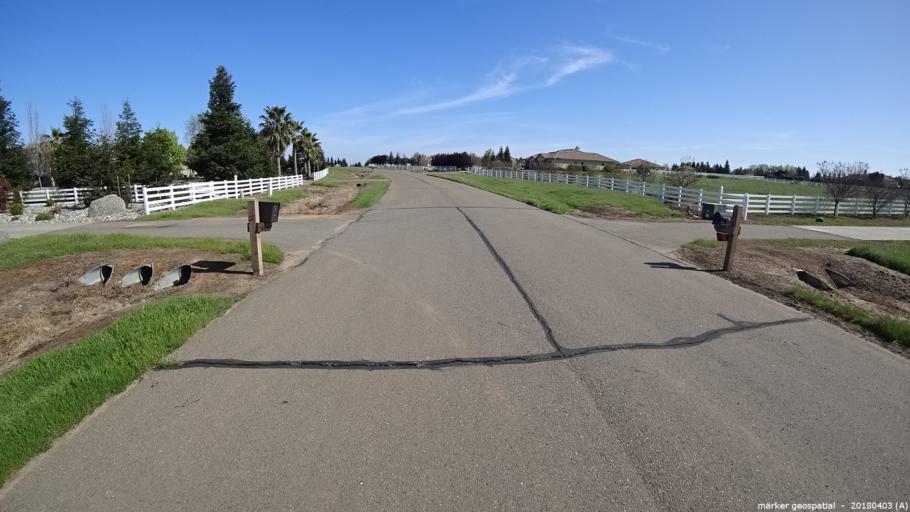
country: US
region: California
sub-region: Sacramento County
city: Wilton
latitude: 38.4108
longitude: -121.1923
